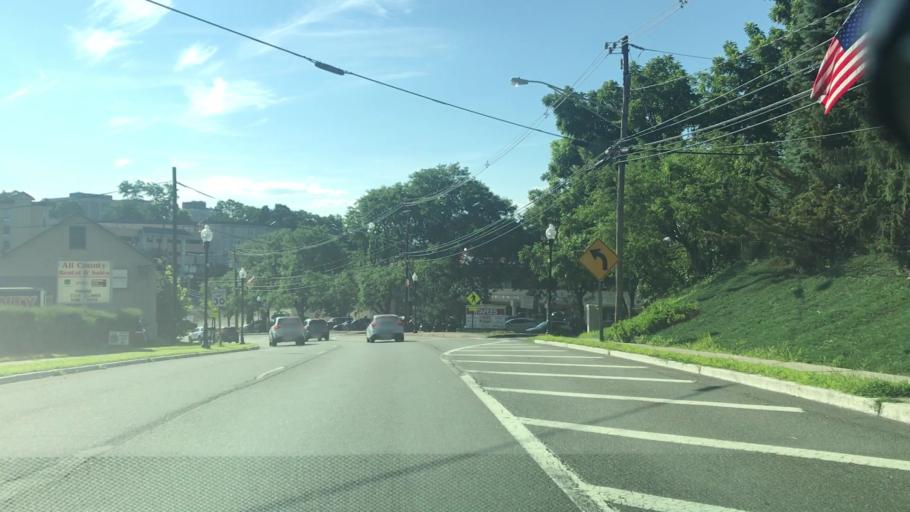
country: US
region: New Jersey
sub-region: Morris County
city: Morristown
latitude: 40.7977
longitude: -74.4727
